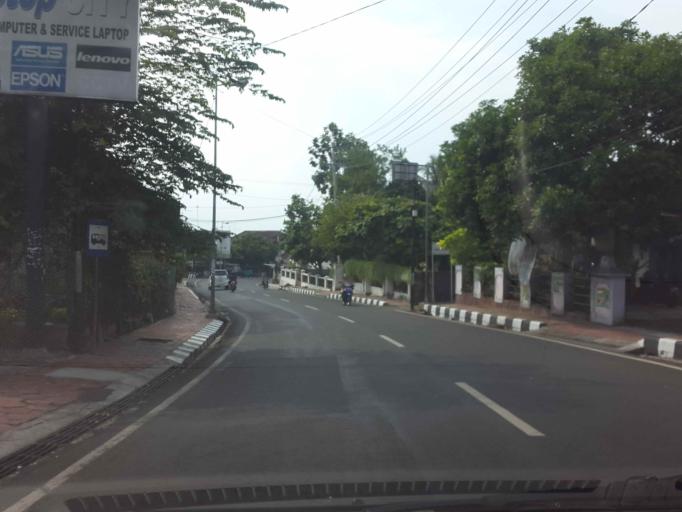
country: ID
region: Central Java
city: Salatiga
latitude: -7.3220
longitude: 110.4957
